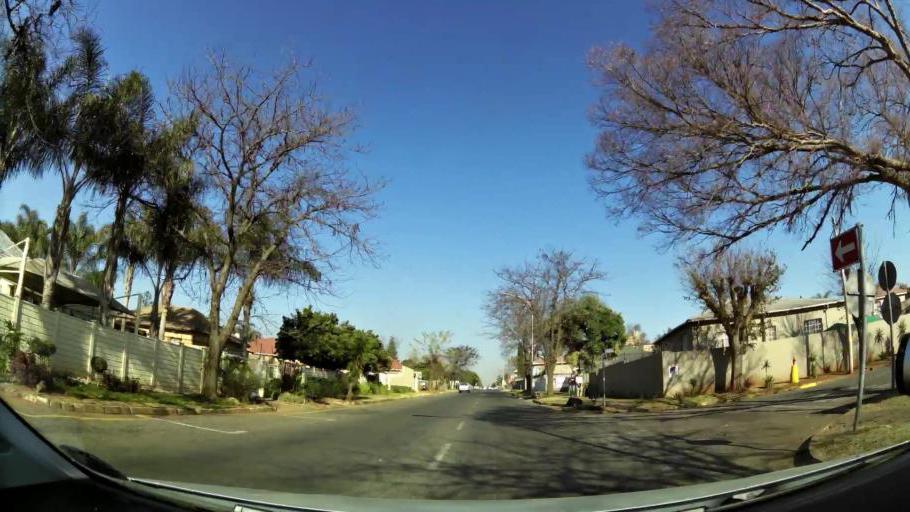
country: ZA
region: Gauteng
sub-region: City of Johannesburg Metropolitan Municipality
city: Modderfontein
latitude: -26.1486
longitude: 28.1597
